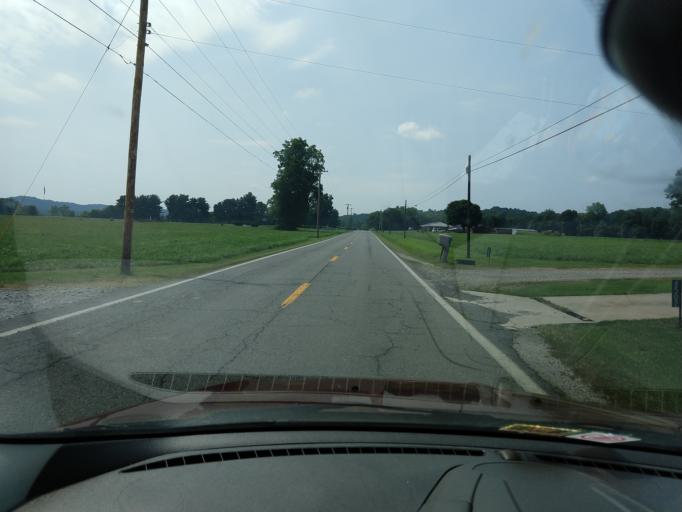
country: US
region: West Virginia
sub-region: Mason County
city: New Haven
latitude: 38.9448
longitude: -81.9198
